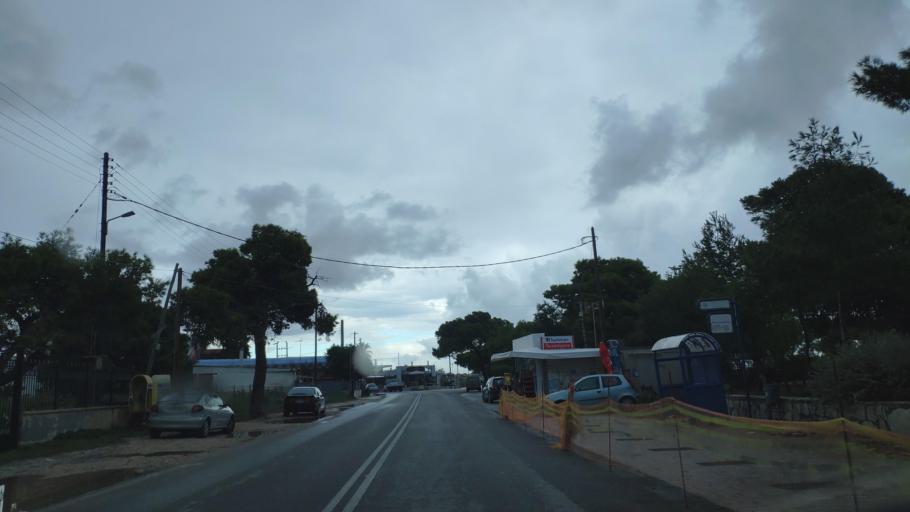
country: GR
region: Attica
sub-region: Nomarchia Anatolikis Attikis
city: Artemida
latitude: 37.9844
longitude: 24.0117
